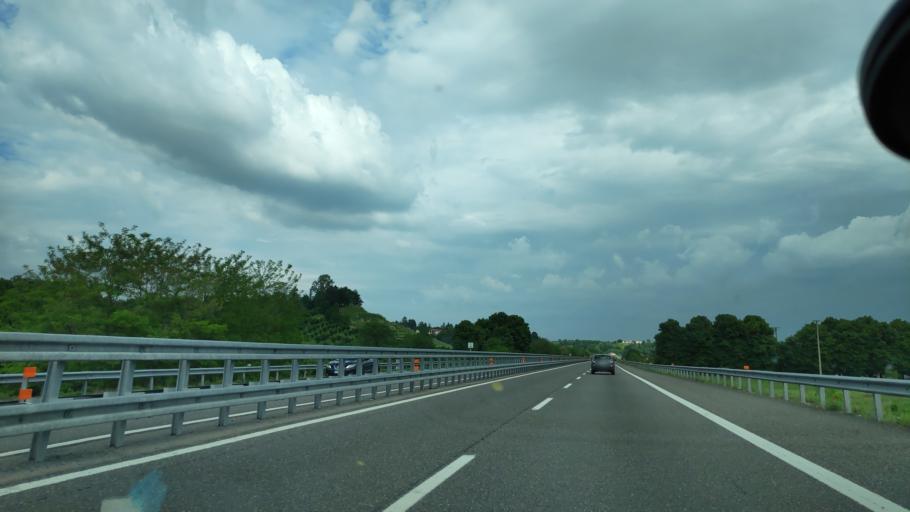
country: IT
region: Piedmont
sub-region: Provincia di Asti
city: Azzano d'Asti
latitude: 44.9080
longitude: 8.2652
